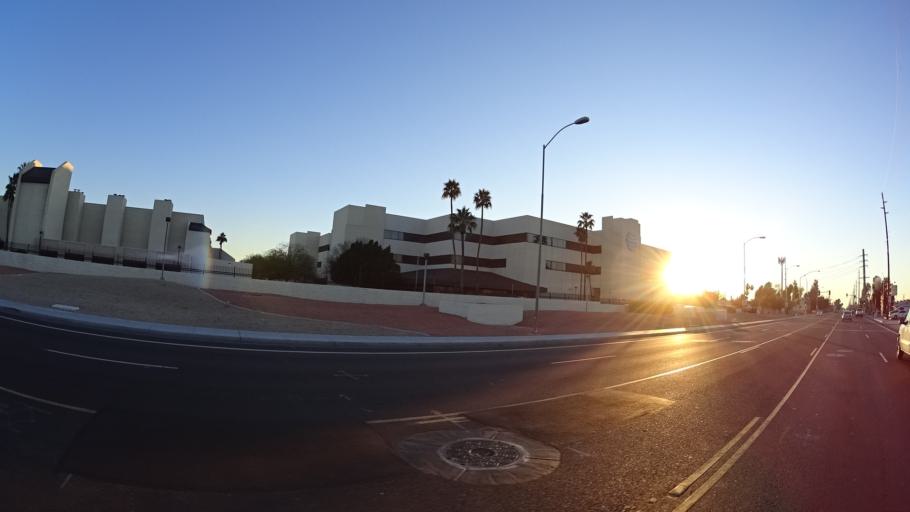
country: US
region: Arizona
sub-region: Maricopa County
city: Mesa
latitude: 33.4222
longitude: -111.8593
